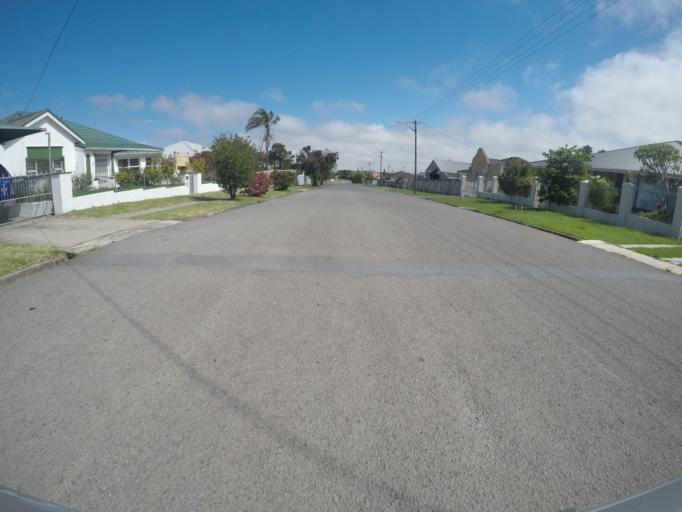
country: ZA
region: Eastern Cape
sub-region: Buffalo City Metropolitan Municipality
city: East London
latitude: -32.9761
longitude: 27.8970
